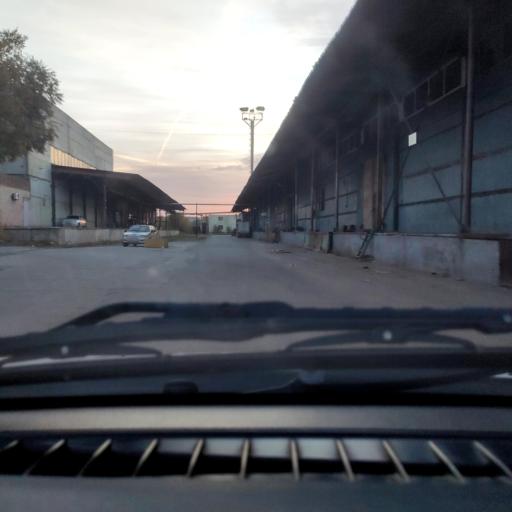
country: RU
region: Samara
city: Zhigulevsk
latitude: 53.4834
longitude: 49.4932
